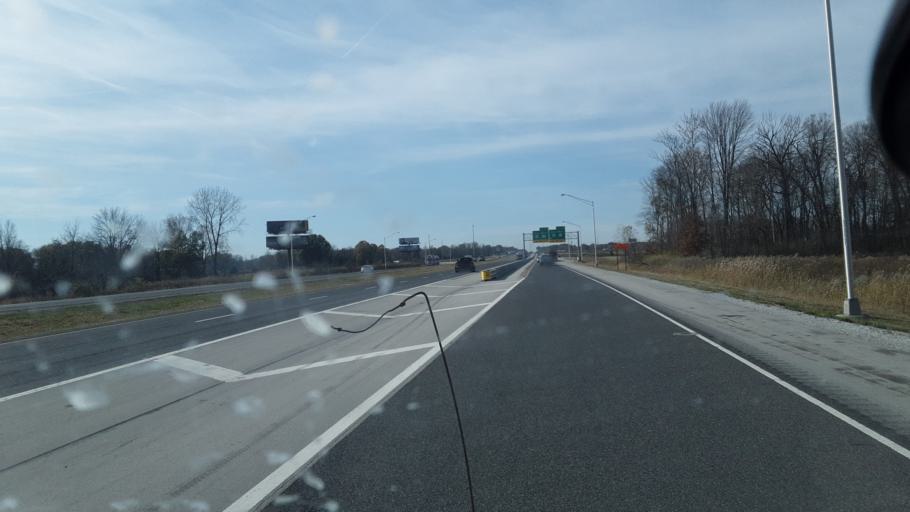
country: US
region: Indiana
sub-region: Vigo County
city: Seelyville
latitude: 39.4309
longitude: -87.3220
